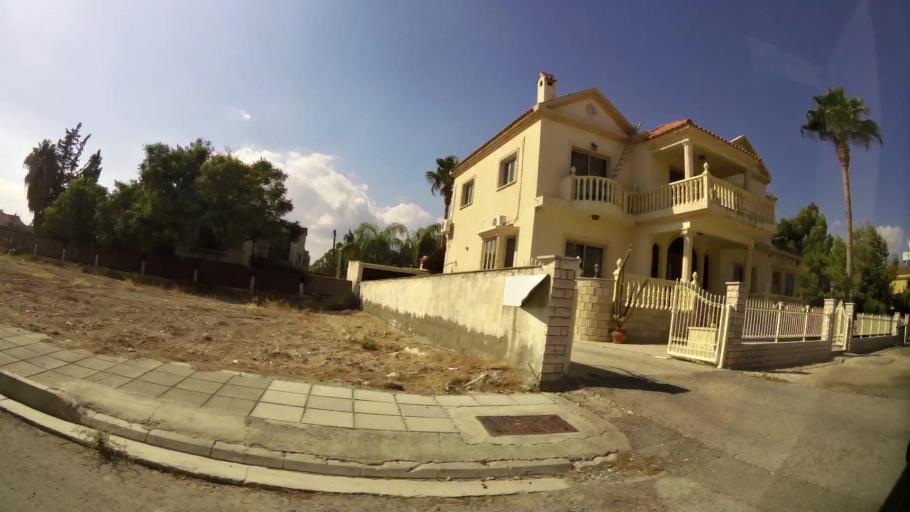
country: CY
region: Larnaka
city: Livadia
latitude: 34.9463
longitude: 33.6312
